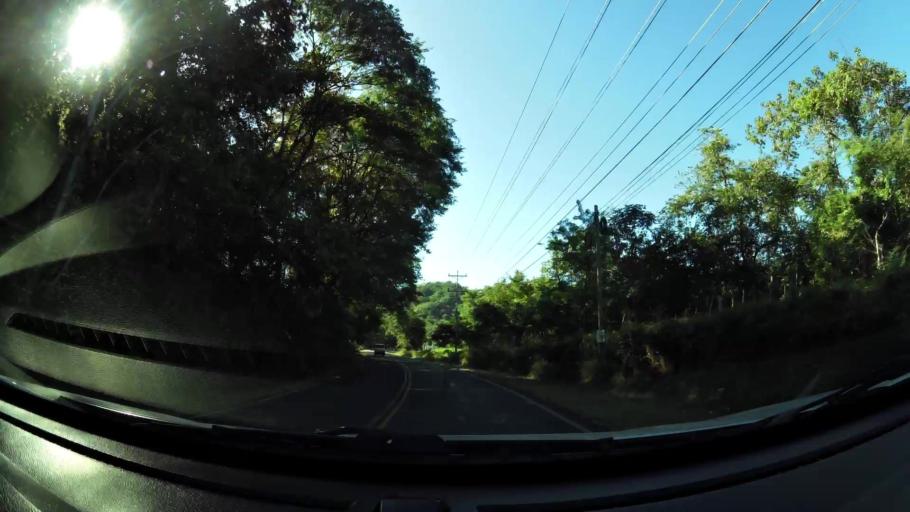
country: CR
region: Guanacaste
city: Belen
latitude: 10.3806
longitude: -85.6210
